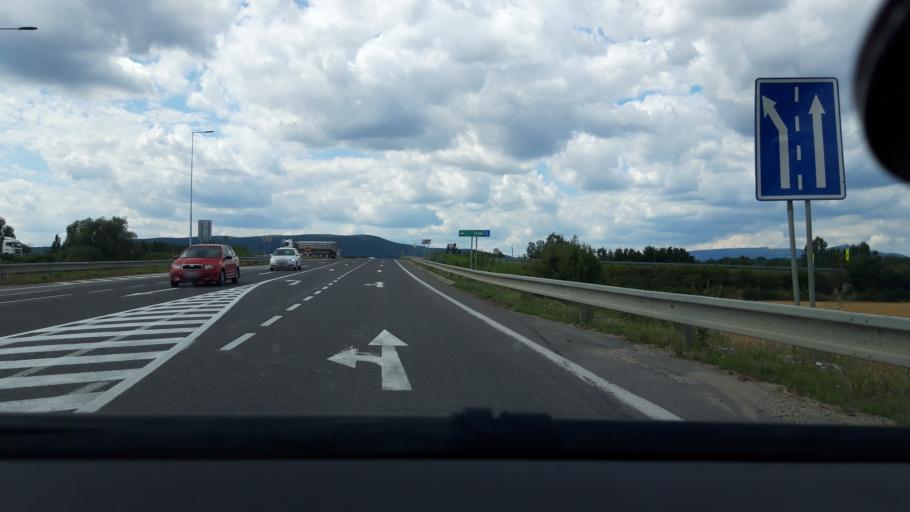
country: SK
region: Trenciansky
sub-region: Okres Nove Mesto nad Vahom
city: Nove Mesto nad Vahom
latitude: 48.7618
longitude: 17.8715
